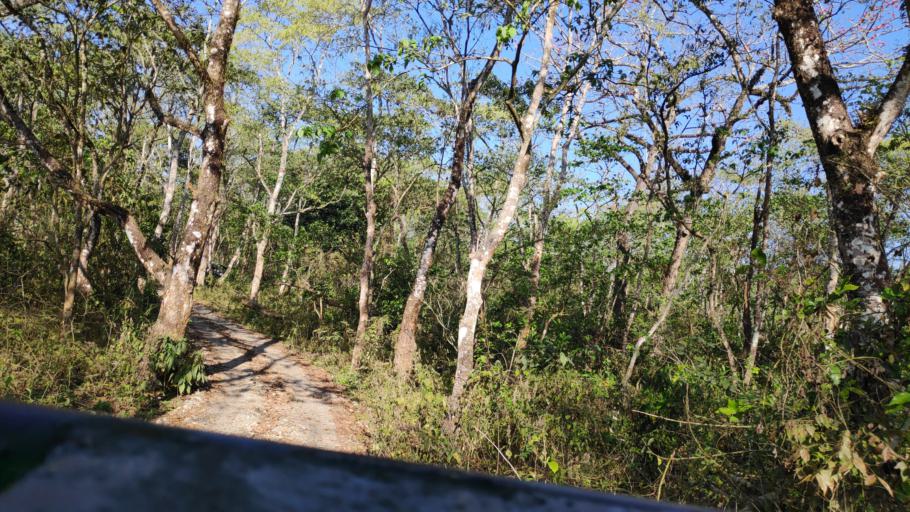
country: NP
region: Central Region
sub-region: Narayani Zone
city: Bharatpur
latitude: 27.5617
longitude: 84.5290
